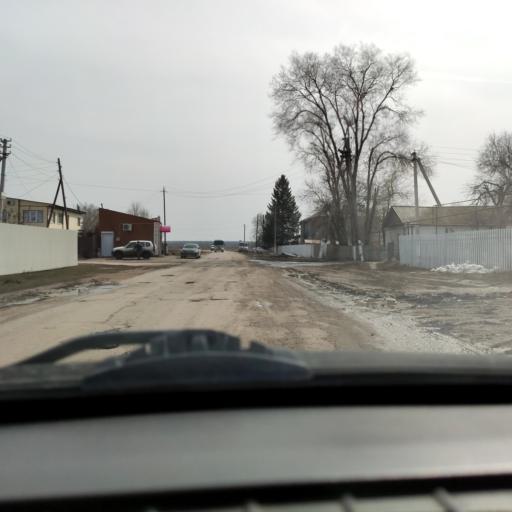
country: RU
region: Samara
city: Smyshlyayevka
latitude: 53.1812
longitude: 50.4622
